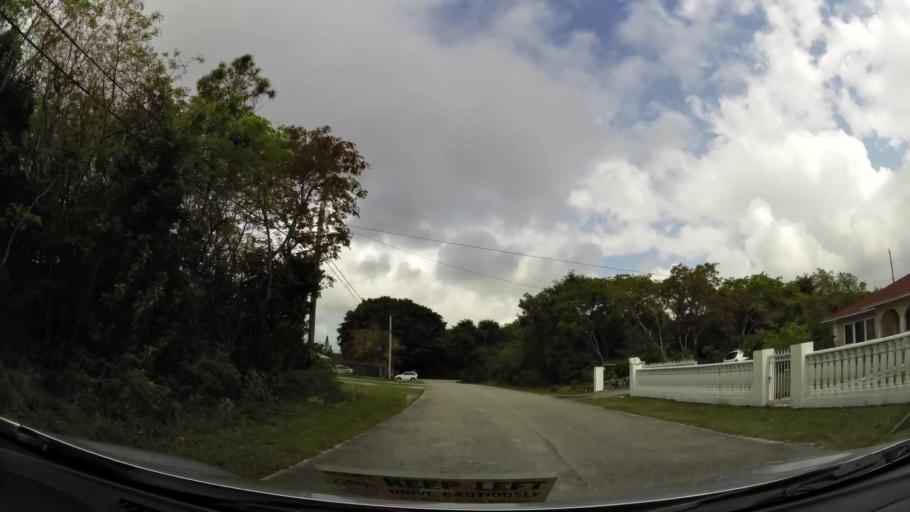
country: BS
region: Freeport
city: Lucaya
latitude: 26.5408
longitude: -78.5965
